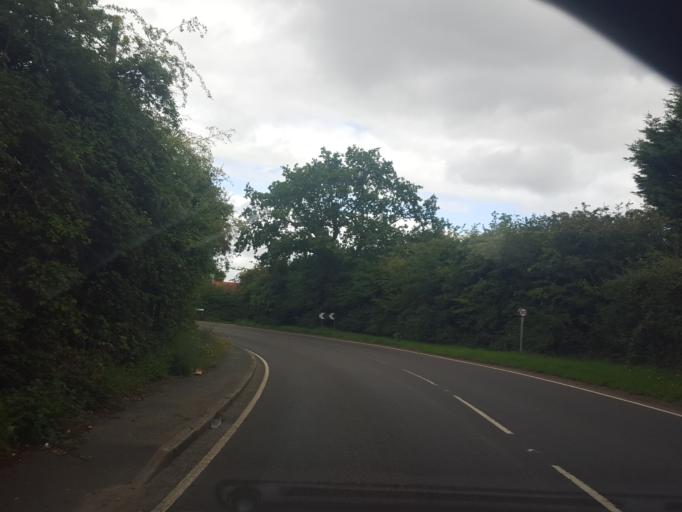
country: GB
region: England
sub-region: Essex
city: Great Bentley
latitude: 51.8767
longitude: 1.0381
